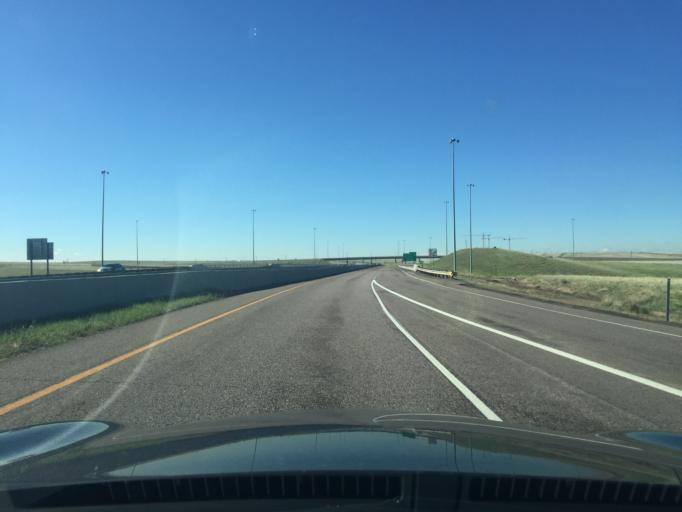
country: US
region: Colorado
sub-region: Adams County
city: Aurora
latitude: 39.8358
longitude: -104.7473
